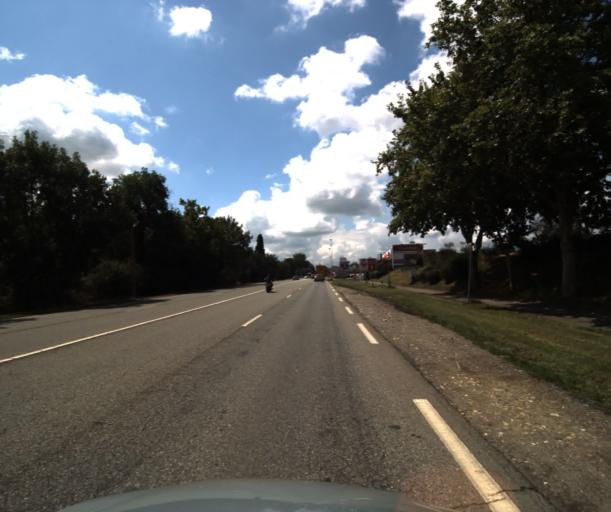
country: FR
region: Midi-Pyrenees
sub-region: Departement de la Haute-Garonne
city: Portet-sur-Garonne
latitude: 43.5424
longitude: 1.4156
